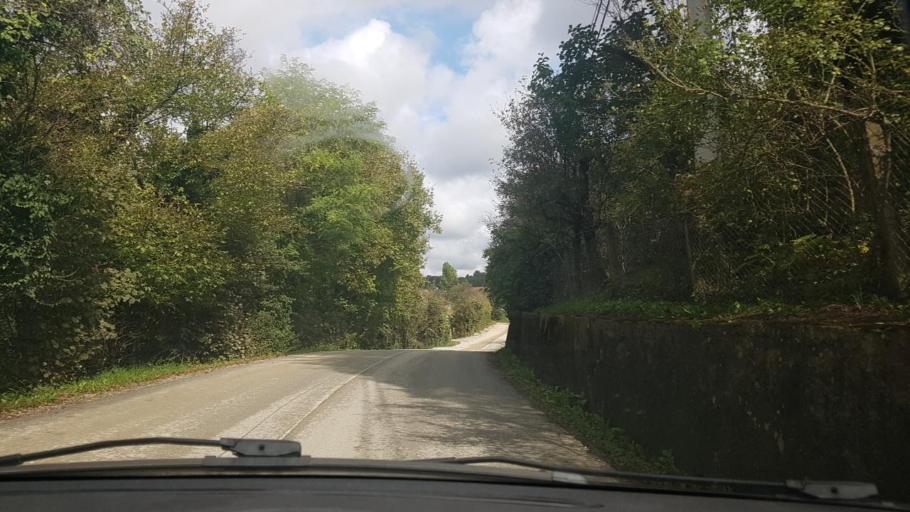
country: HR
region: Zagrebacka
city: Pojatno
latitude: 45.9366
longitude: 15.7262
